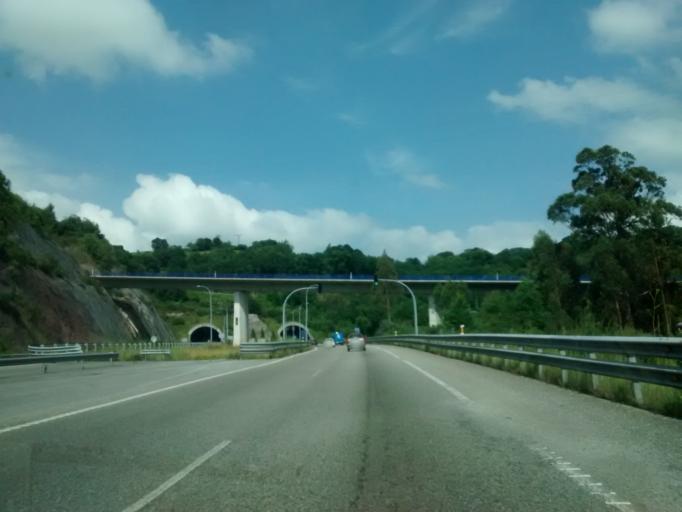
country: ES
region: Asturias
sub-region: Province of Asturias
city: Sama
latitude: 43.3385
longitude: -5.7101
